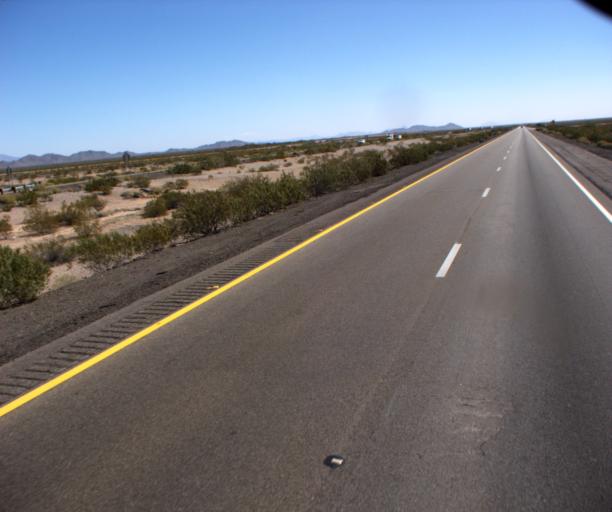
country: US
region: Arizona
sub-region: La Paz County
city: Salome
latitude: 33.6087
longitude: -113.6196
